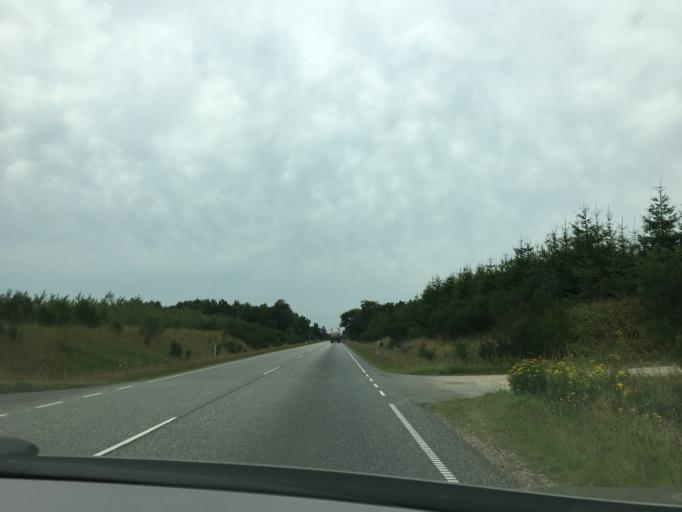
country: DK
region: Central Jutland
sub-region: Herning Kommune
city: Sunds
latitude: 56.3797
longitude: 8.9879
